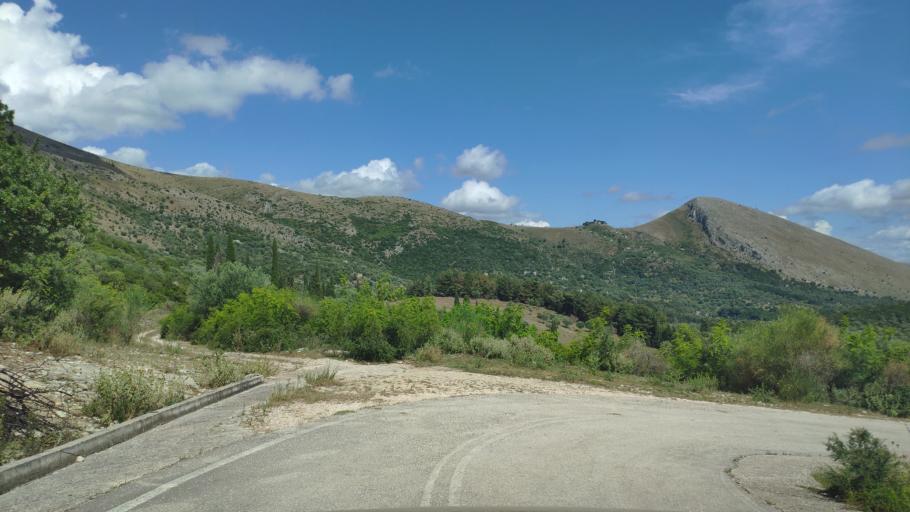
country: AL
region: Vlore
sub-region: Rrethi i Sarandes
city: Konispol
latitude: 39.6317
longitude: 20.2117
